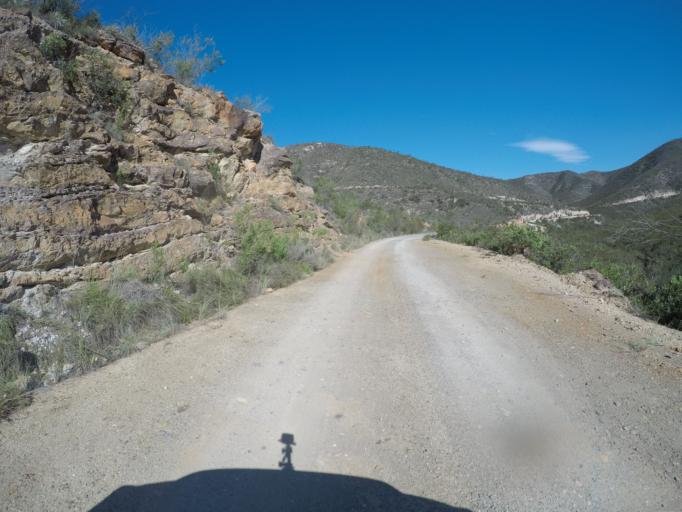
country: ZA
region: Eastern Cape
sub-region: Cacadu District Municipality
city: Kareedouw
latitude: -33.6531
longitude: 24.5027
